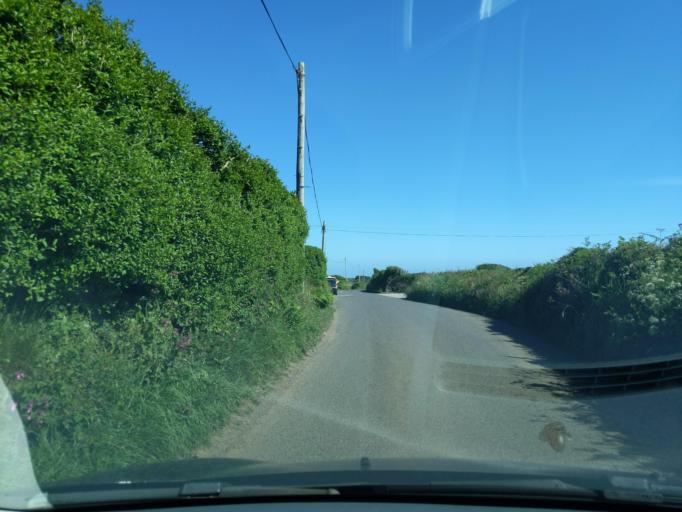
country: GB
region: England
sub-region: Cornwall
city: St. Buryan
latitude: 50.0668
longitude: -5.6049
